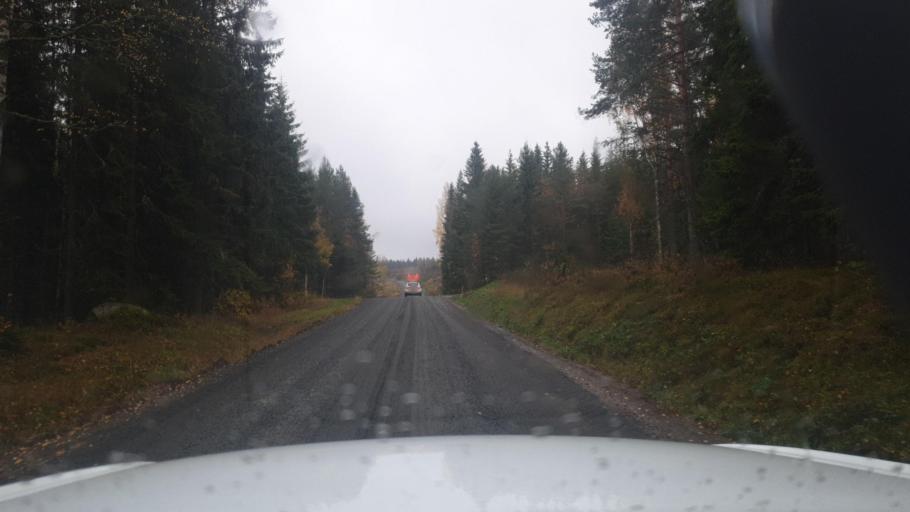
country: SE
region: Vaermland
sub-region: Torsby Kommun
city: Torsby
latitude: 60.1806
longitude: 12.6455
